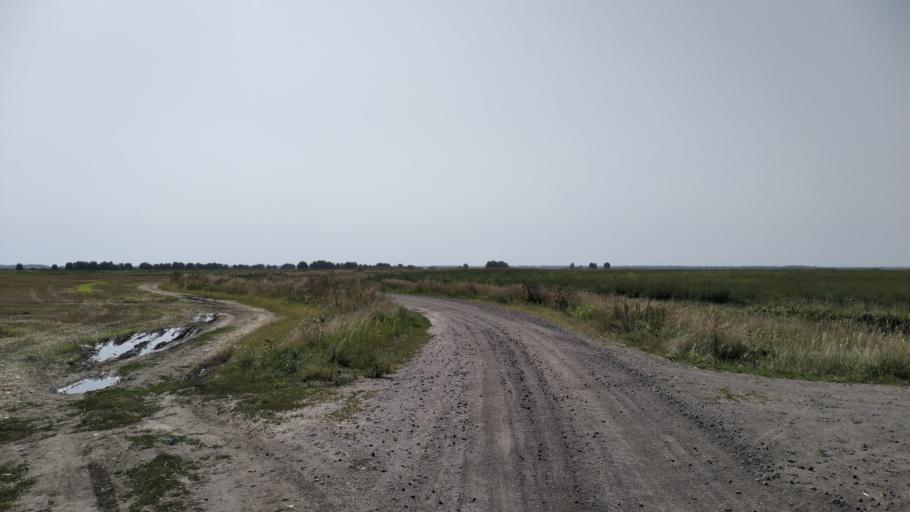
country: BY
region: Brest
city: Davyd-Haradok
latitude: 52.0087
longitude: 27.1661
